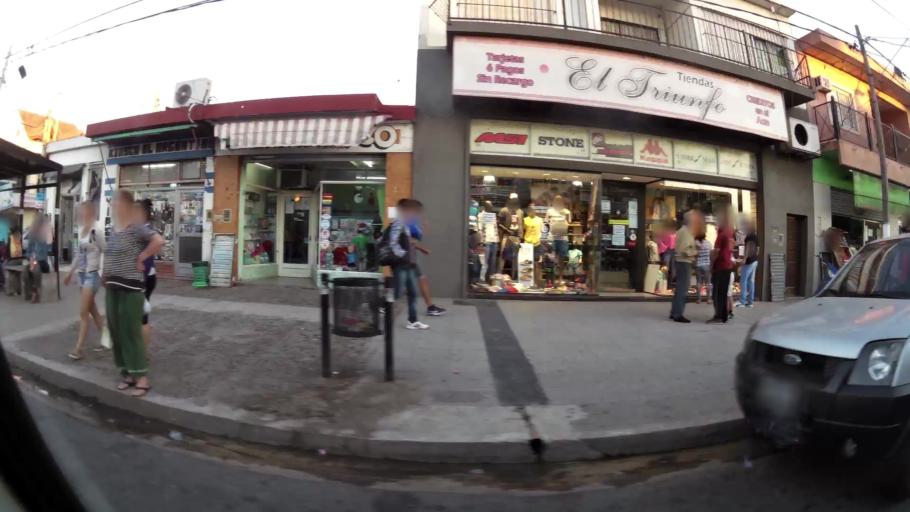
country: AR
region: Buenos Aires
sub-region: Partido de Quilmes
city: Quilmes
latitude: -34.8094
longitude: -58.1871
